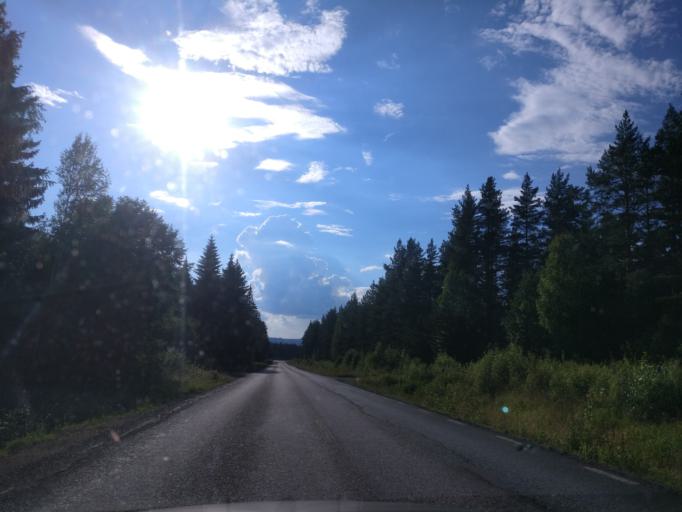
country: SE
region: Dalarna
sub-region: Ludvika Kommun
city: Ludvika
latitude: 60.2654
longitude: 15.0415
